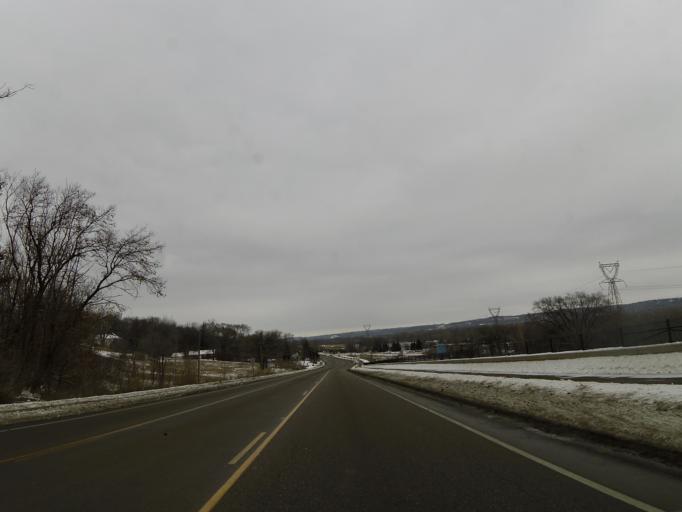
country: US
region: Minnesota
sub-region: Dakota County
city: Inver Grove Heights
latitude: 44.8492
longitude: -93.0202
